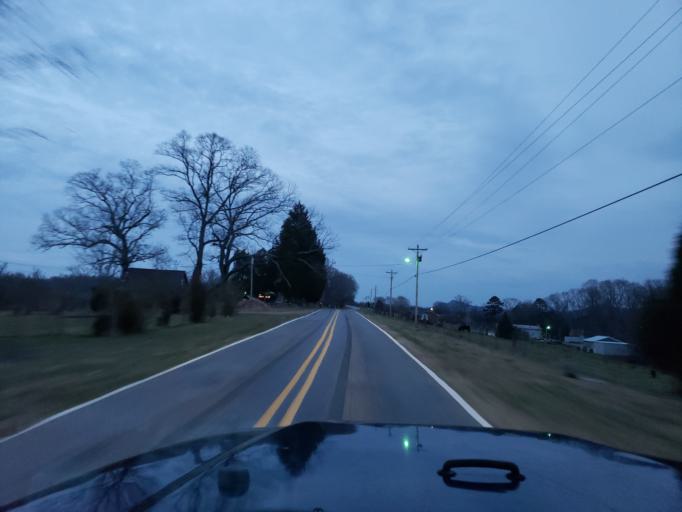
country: US
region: North Carolina
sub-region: Cleveland County
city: White Plains
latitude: 35.1743
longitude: -81.3972
